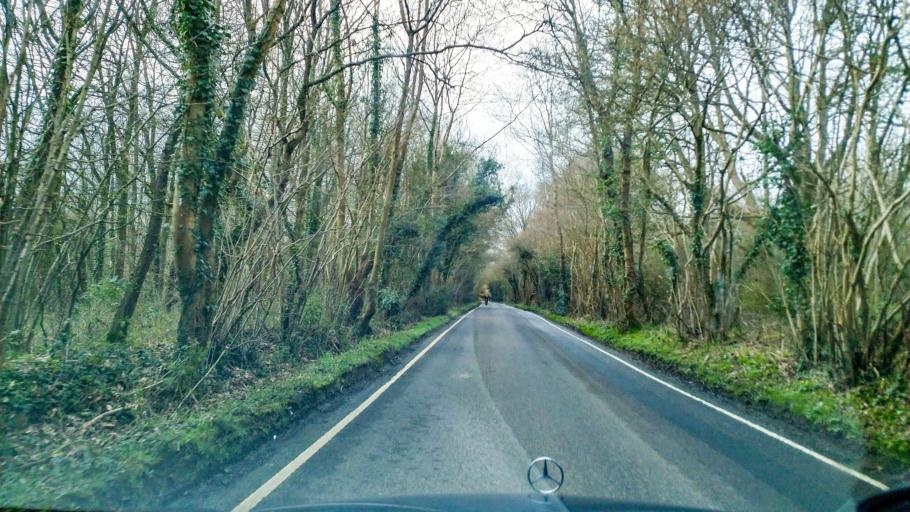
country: GB
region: England
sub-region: Surrey
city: Dorking
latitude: 51.2131
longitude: -0.3195
